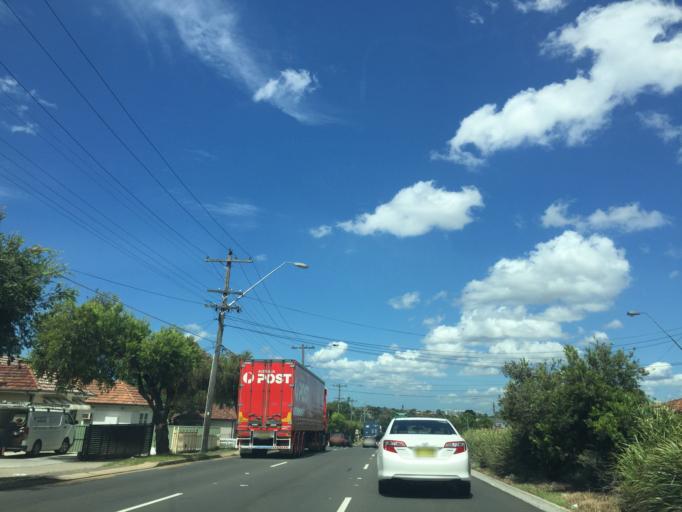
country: AU
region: New South Wales
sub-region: Canterbury
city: Lakemba
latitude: -33.9120
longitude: 151.0635
